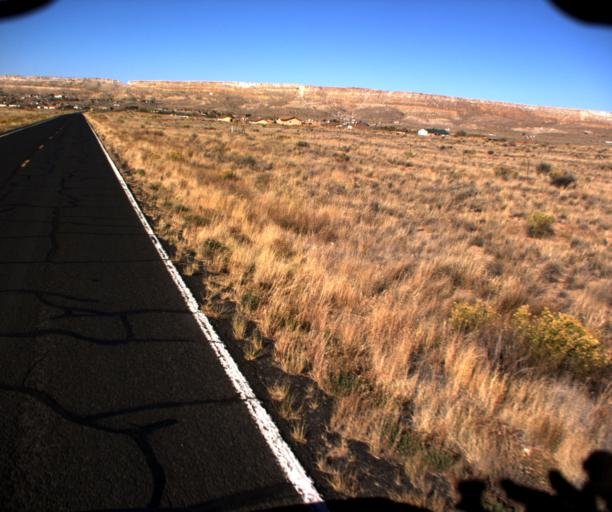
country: US
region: Arizona
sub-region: Navajo County
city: First Mesa
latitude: 35.8403
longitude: -110.3494
